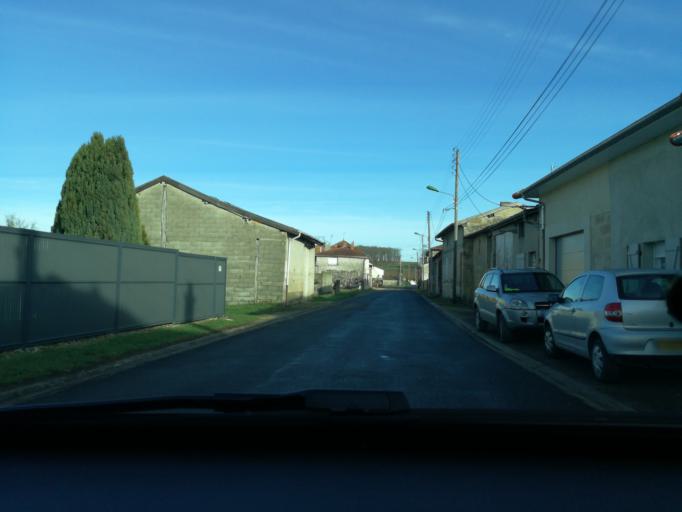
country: FR
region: Lorraine
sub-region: Departement de la Meuse
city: Revigny-sur-Ornain
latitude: 48.8240
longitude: 5.0445
